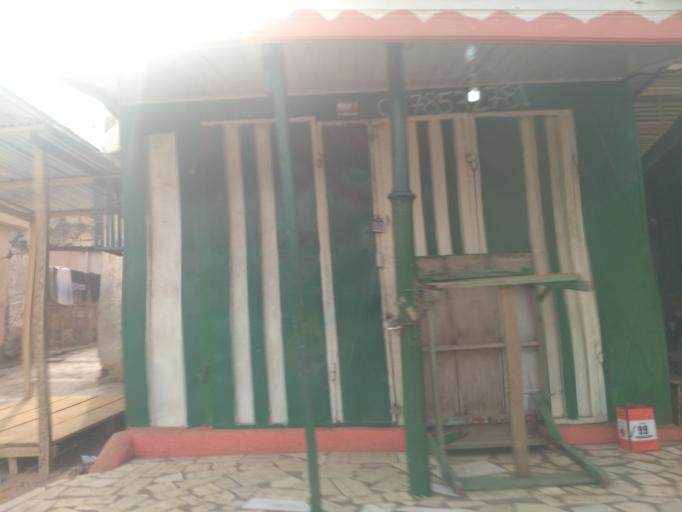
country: GH
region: Ashanti
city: Kumasi
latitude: 6.7012
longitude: -1.6312
